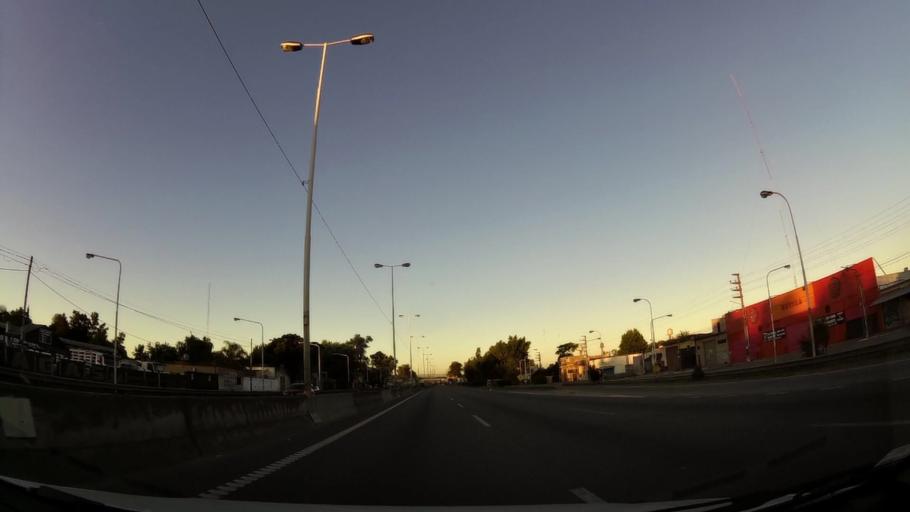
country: AR
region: Buenos Aires
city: Pontevedra
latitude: -34.7886
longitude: -58.6289
